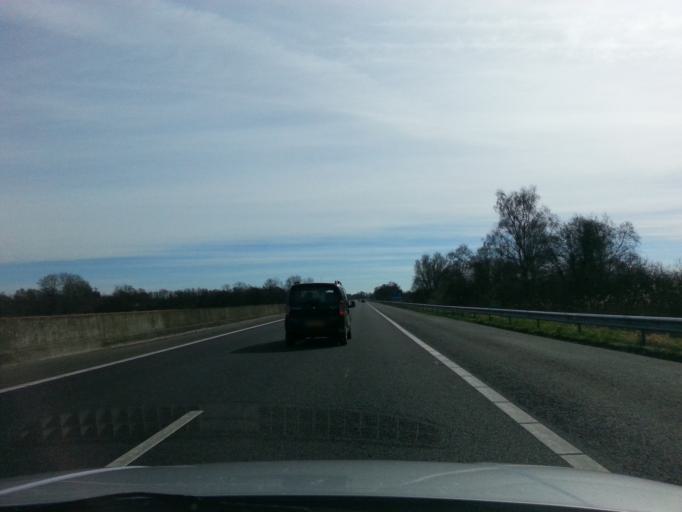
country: NL
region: Groningen
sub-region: Gemeente Haren
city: Haren
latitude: 53.1581
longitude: 6.5962
